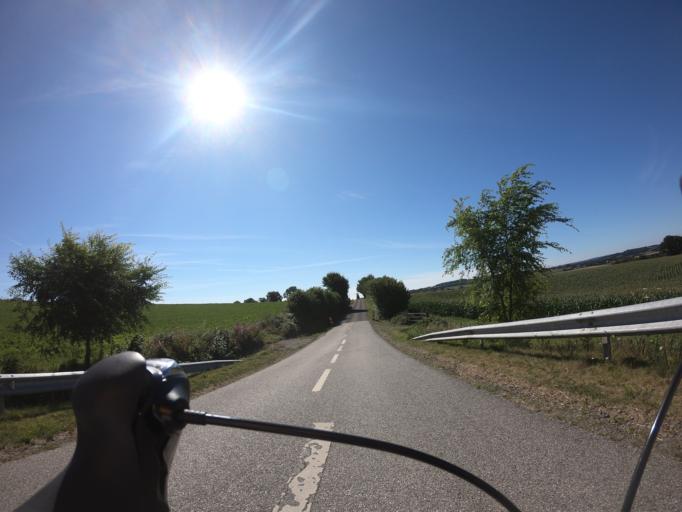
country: FR
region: Pays de la Loire
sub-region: Departement de la Mayenne
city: Pre-en-Pail
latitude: 48.5640
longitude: -0.1371
